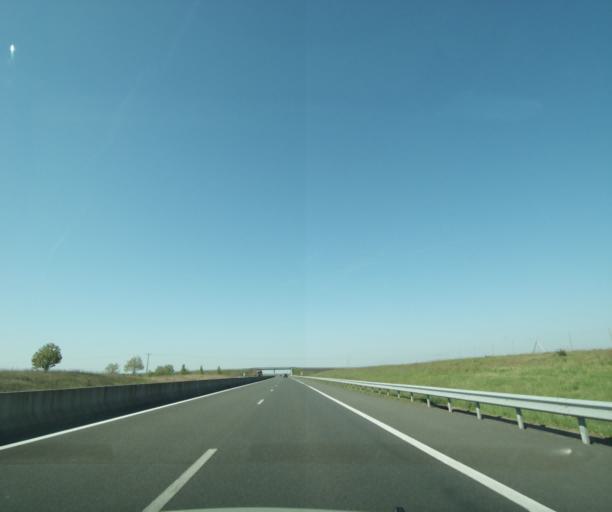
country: FR
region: Centre
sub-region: Departement du Loiret
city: Ascheres-le-Marche
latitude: 48.0778
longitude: 1.9792
